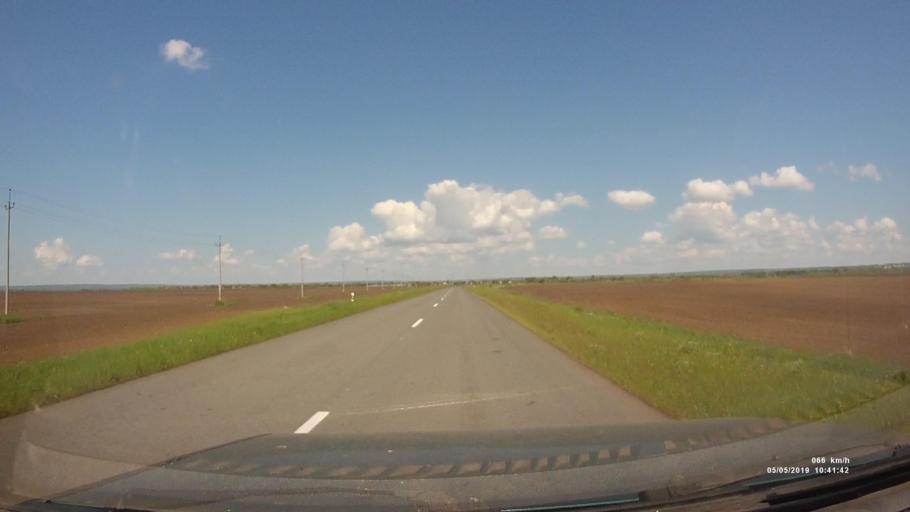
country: RU
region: Rostov
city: Ust'-Donetskiy
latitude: 47.5928
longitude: 40.8399
